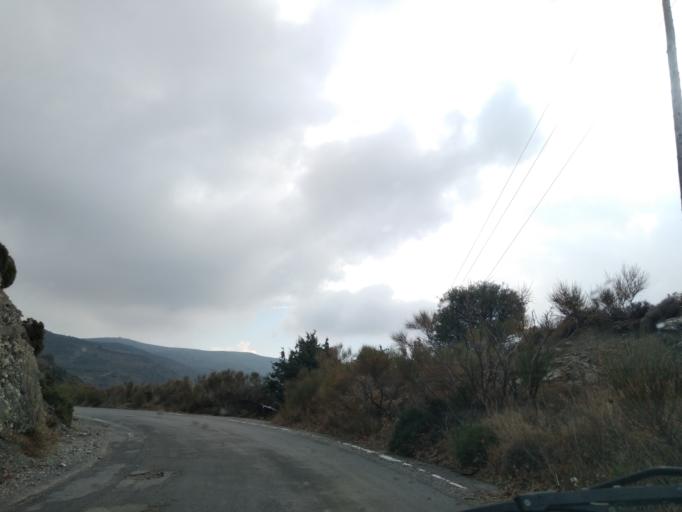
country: GR
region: Crete
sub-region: Nomos Lasithiou
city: Siteia
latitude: 35.1478
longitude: 26.0201
